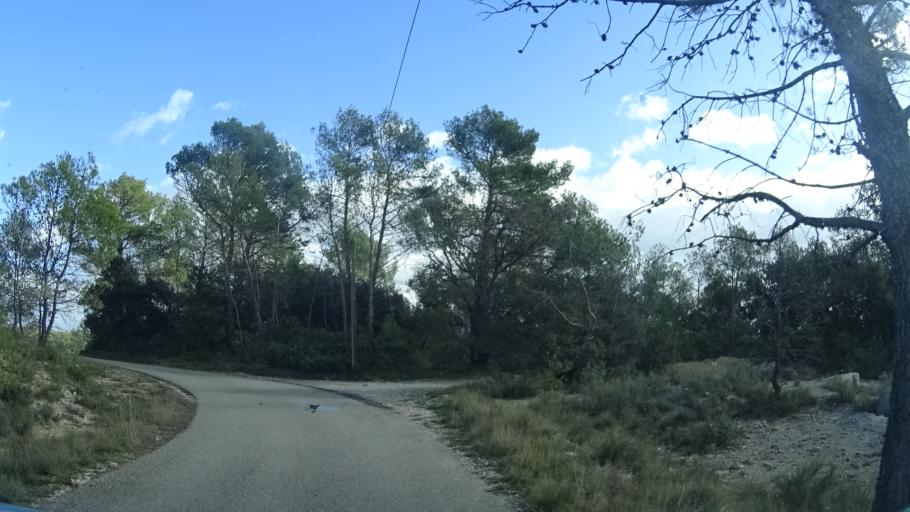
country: FR
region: Languedoc-Roussillon
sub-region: Departement de l'Herault
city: Claret
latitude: 43.8392
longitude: 3.8783
